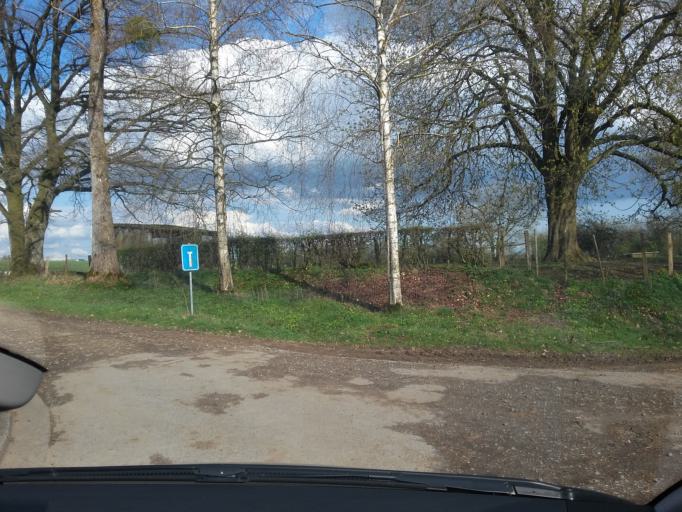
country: BE
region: Wallonia
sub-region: Province du Luxembourg
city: Florenville
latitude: 49.7098
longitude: 5.3060
